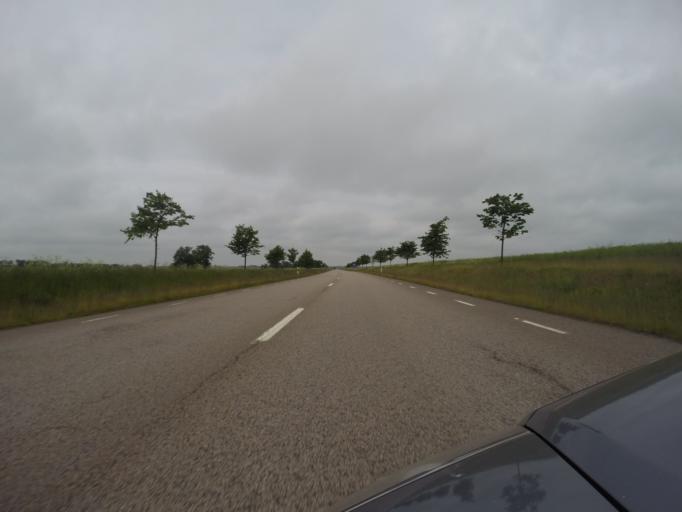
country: SE
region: Skane
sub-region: Bjuvs Kommun
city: Bjuv
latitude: 56.0121
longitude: 12.9194
